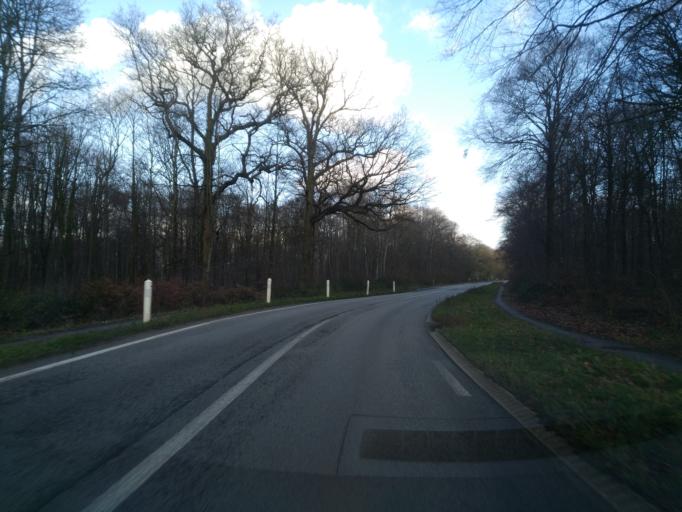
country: FR
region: Ile-de-France
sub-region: Departement des Yvelines
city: Fourqueux
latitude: 48.8771
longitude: 2.0509
